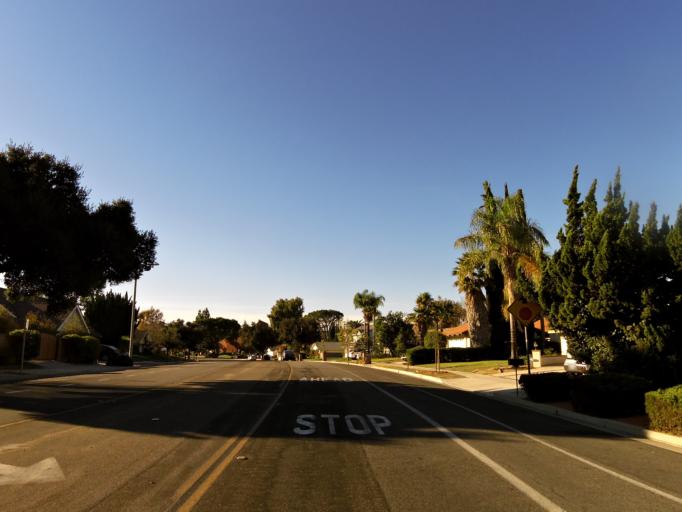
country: US
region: California
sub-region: Ventura County
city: Thousand Oaks
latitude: 34.2181
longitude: -118.8735
